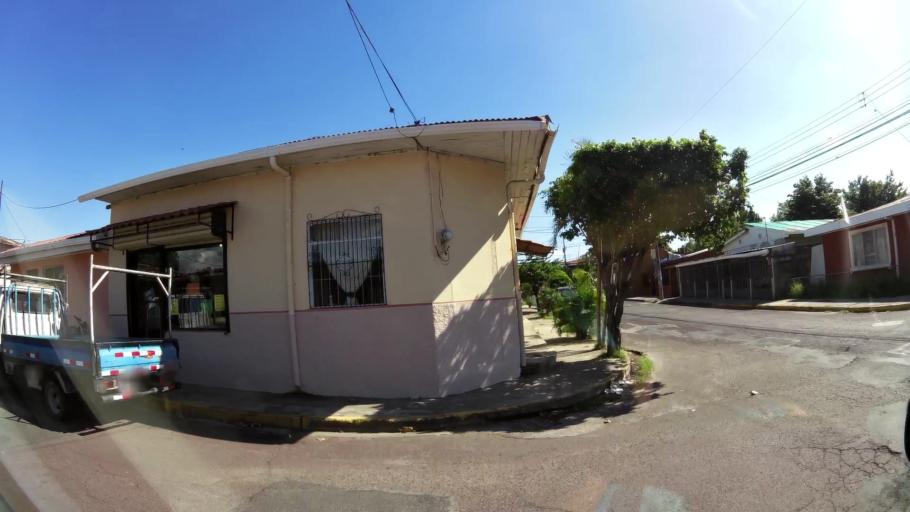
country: CR
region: Guanacaste
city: Liberia
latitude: 10.6326
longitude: -85.4409
